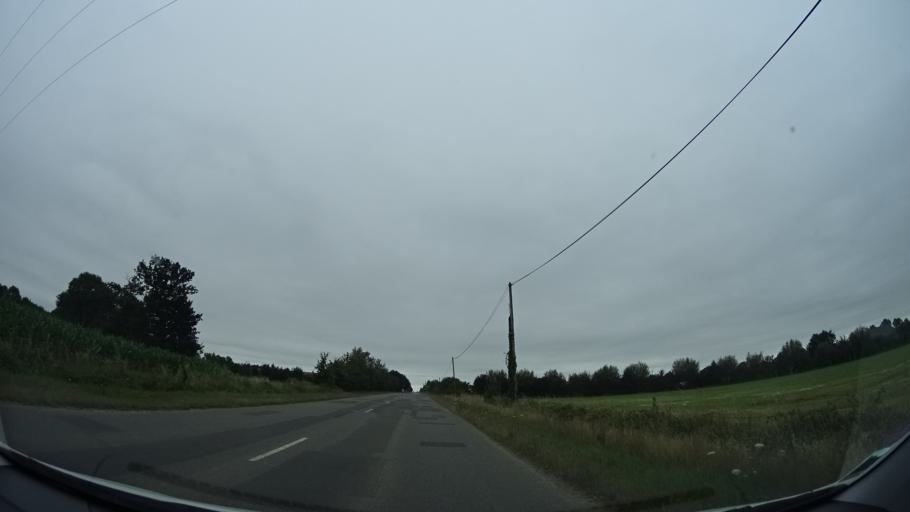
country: FR
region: Brittany
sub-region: Departement d'Ille-et-Vilaine
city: La Meziere
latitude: 48.2264
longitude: -1.7539
